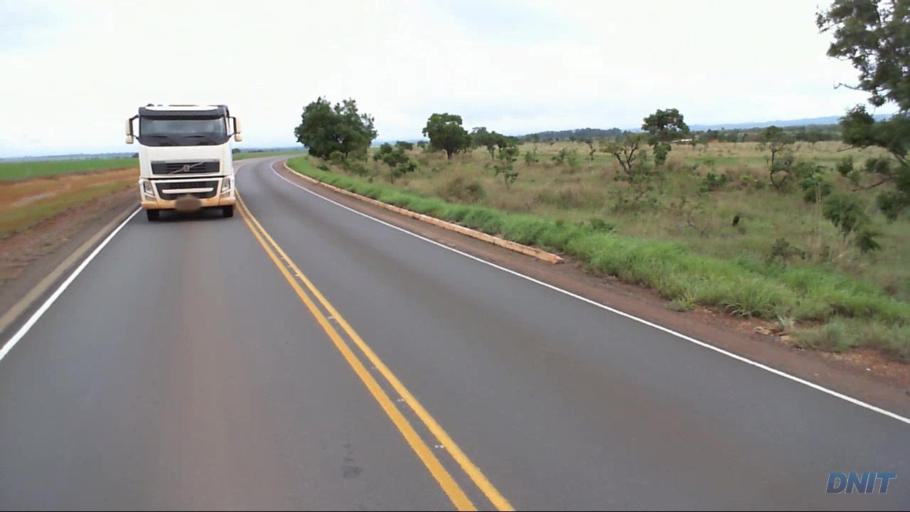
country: BR
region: Goias
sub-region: Padre Bernardo
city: Padre Bernardo
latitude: -15.3420
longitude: -48.2342
